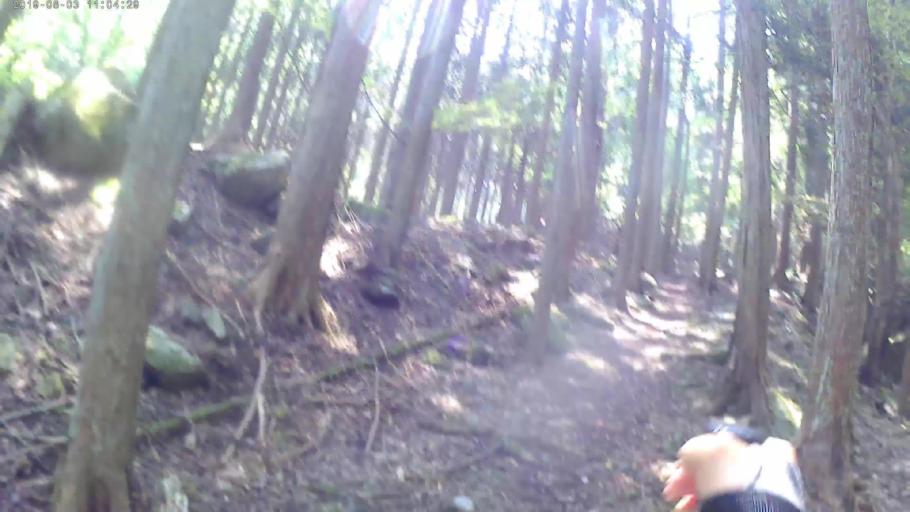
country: JP
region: Yamanashi
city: Enzan
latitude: 35.6183
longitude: 138.7742
